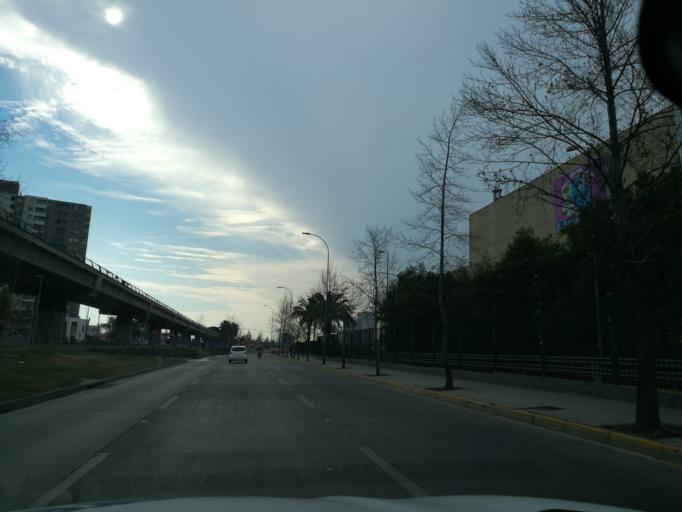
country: CL
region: Santiago Metropolitan
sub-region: Provincia de Santiago
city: Villa Presidente Frei, Nunoa, Santiago, Chile
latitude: -33.5107
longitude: -70.6088
